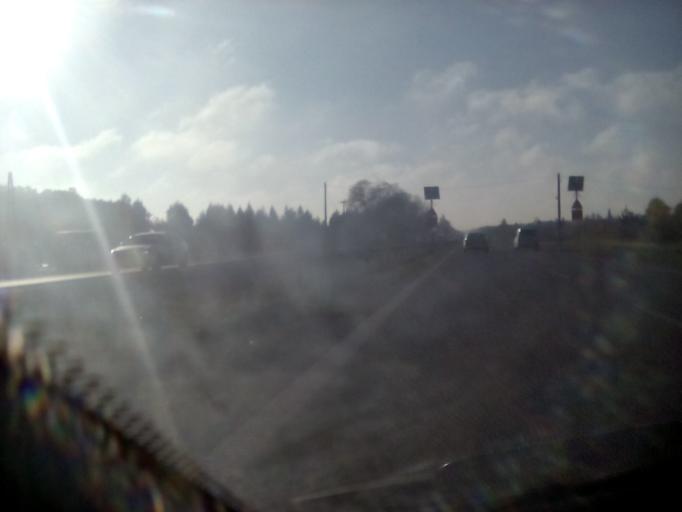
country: PL
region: Masovian Voivodeship
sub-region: Powiat piaseczynski
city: Tarczyn
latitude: 51.9353
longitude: 20.8475
